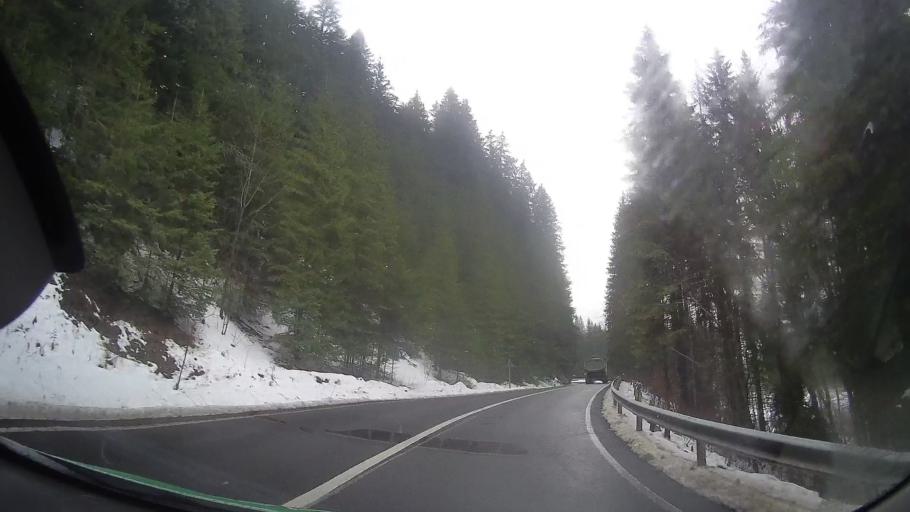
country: RO
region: Neamt
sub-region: Comuna Bicaz Chei
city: Bicaz Chei
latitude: 46.7801
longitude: 25.7837
